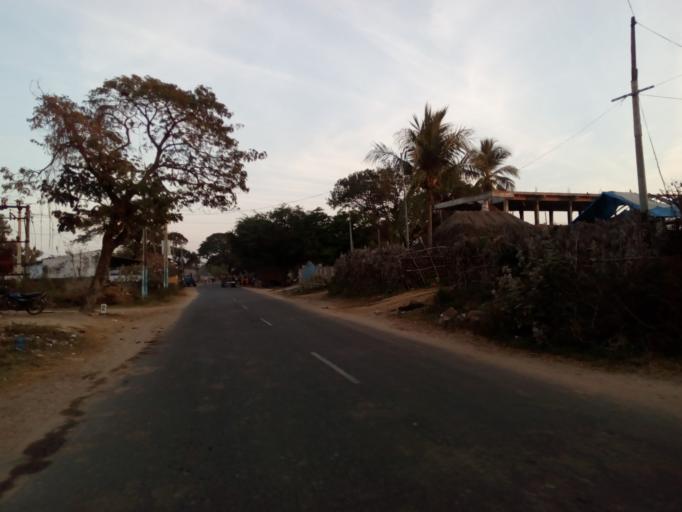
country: IN
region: Andhra Pradesh
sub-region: Prakasam
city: Vetapalem
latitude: 15.7250
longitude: 80.2533
